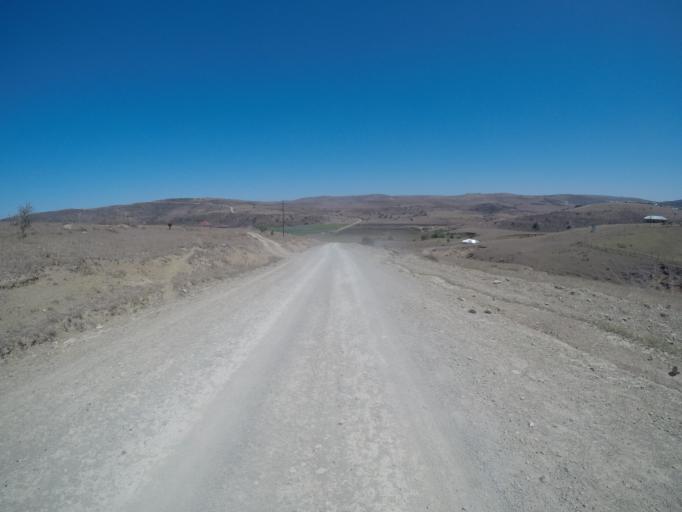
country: ZA
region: Eastern Cape
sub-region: OR Tambo District Municipality
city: Mthatha
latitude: -31.8647
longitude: 28.8725
